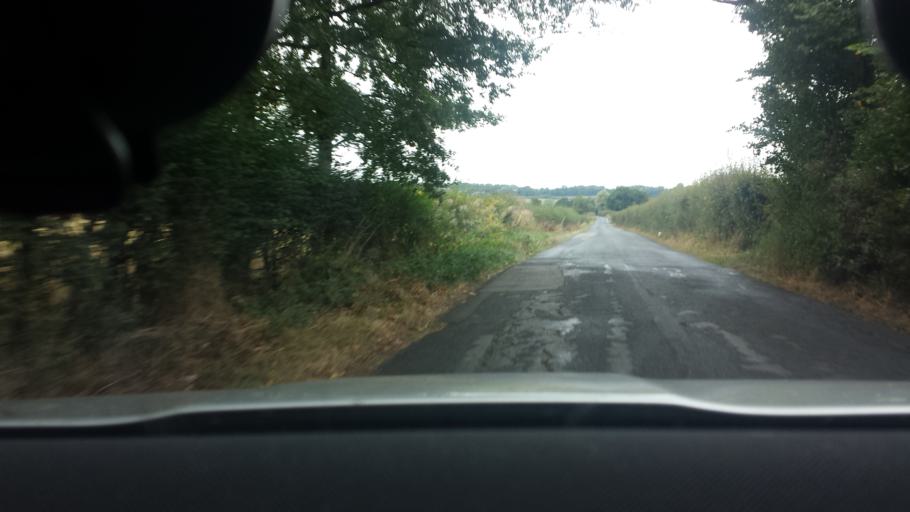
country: GB
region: England
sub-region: Kent
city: Staplehurst
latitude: 51.1978
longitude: 0.5544
